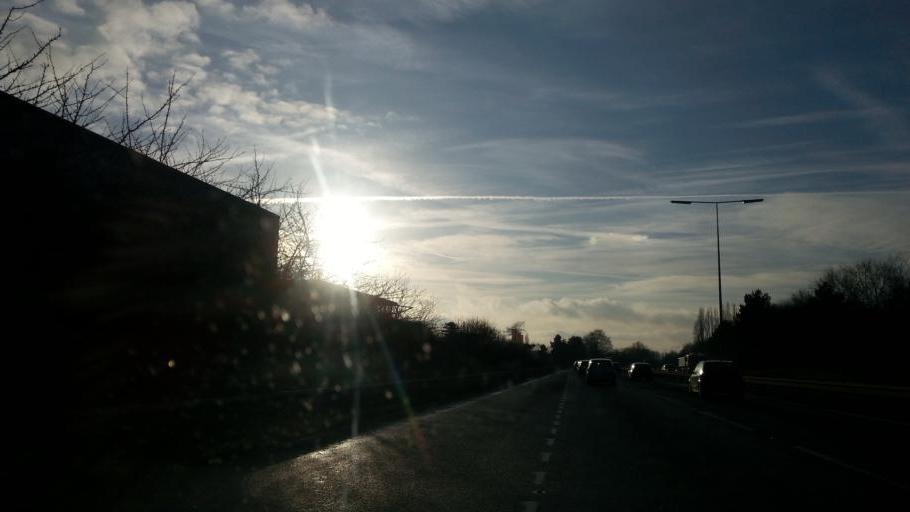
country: GB
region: England
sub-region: Northamptonshire
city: Earls Barton
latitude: 52.2486
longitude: -0.8144
